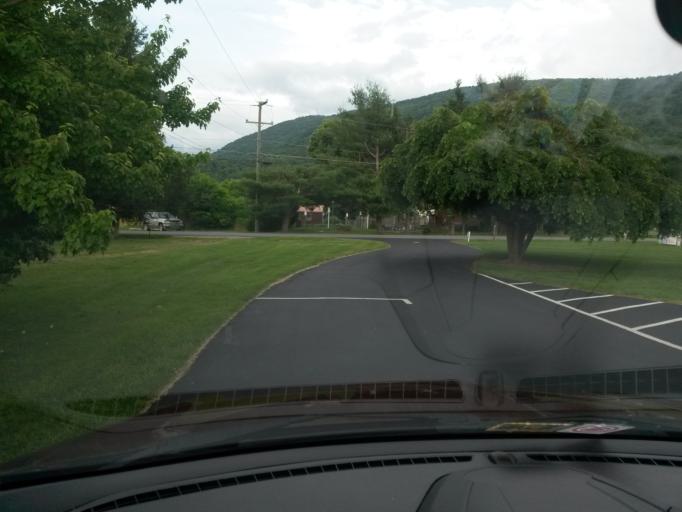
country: US
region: Virginia
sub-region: City of Covington
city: Fairlawn
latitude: 37.7652
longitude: -79.9679
